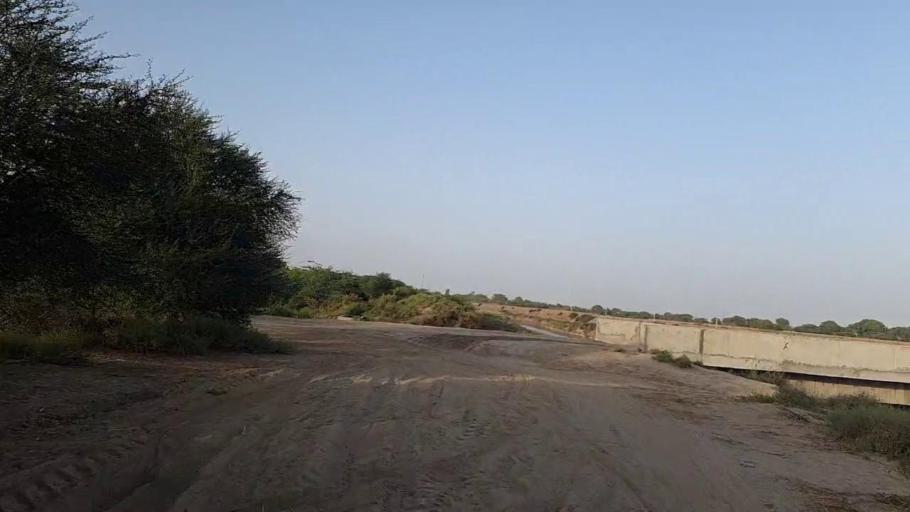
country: PK
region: Sindh
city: Jati
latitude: 24.4151
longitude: 68.1867
